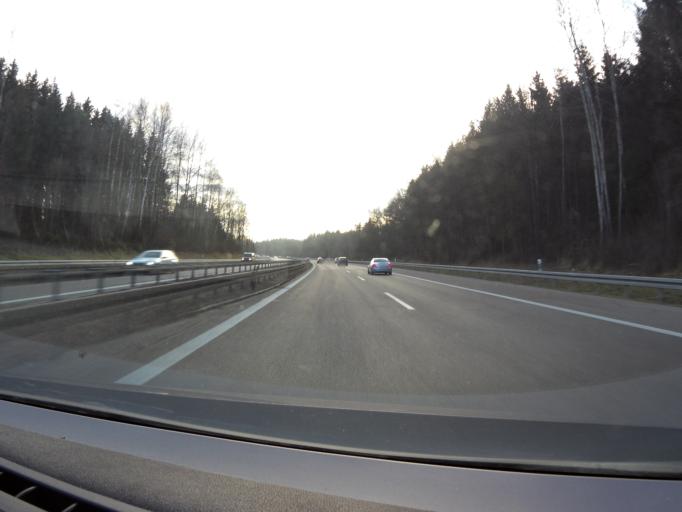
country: DE
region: Bavaria
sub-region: Upper Bavaria
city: Berg
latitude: 47.8697
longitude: 11.3940
